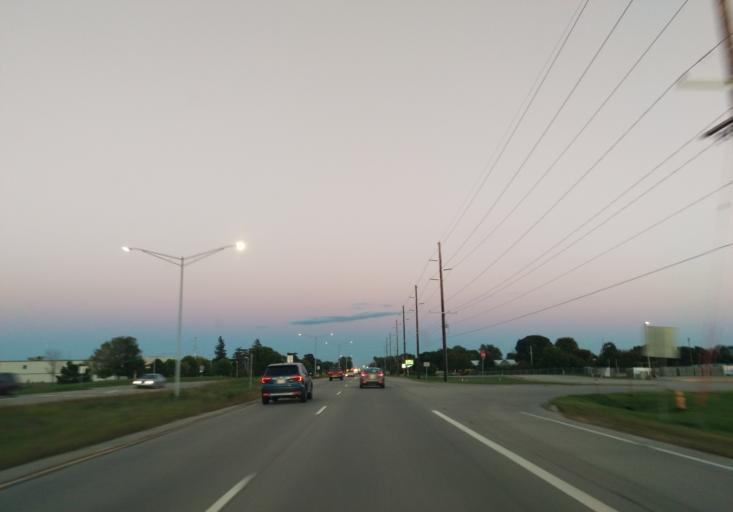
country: US
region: Wisconsin
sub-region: Rock County
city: Janesville
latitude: 42.7242
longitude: -89.0113
